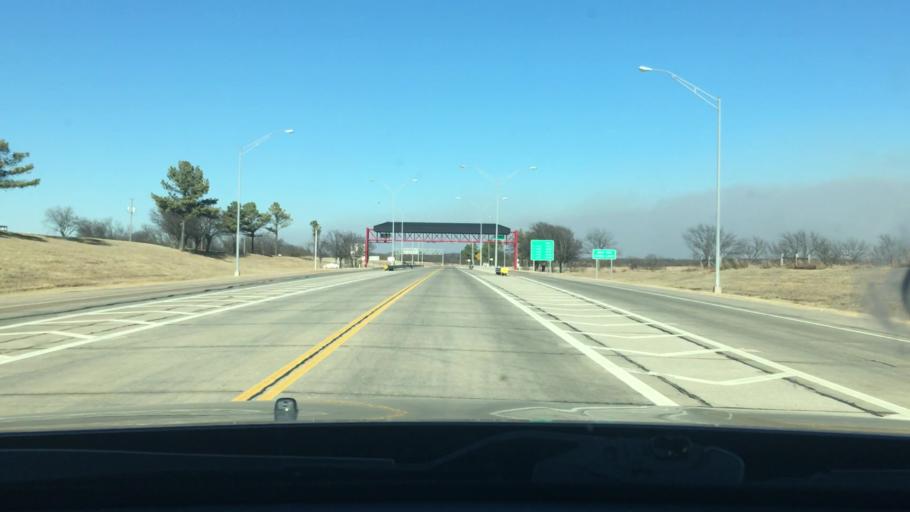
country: US
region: Oklahoma
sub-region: Murray County
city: Sulphur
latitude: 34.5654
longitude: -96.9311
